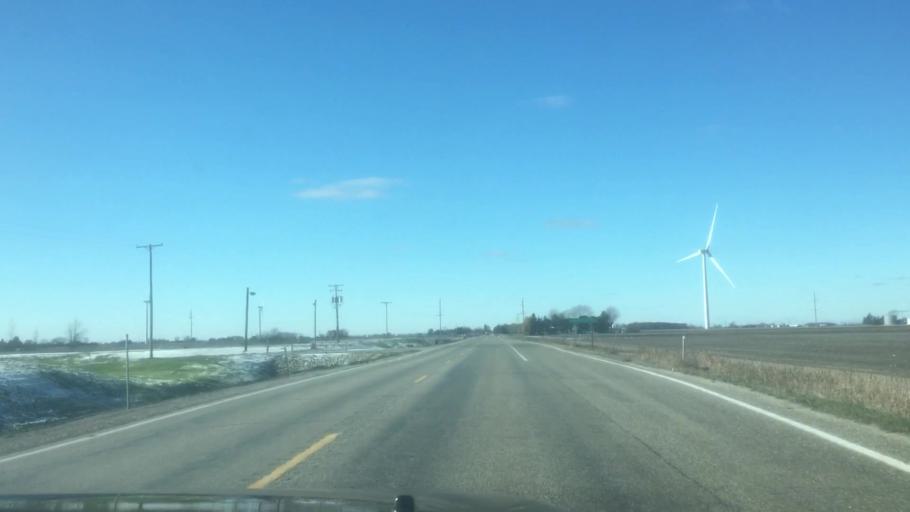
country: US
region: Michigan
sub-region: Tuscola County
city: Reese
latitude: 43.5227
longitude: -83.6590
